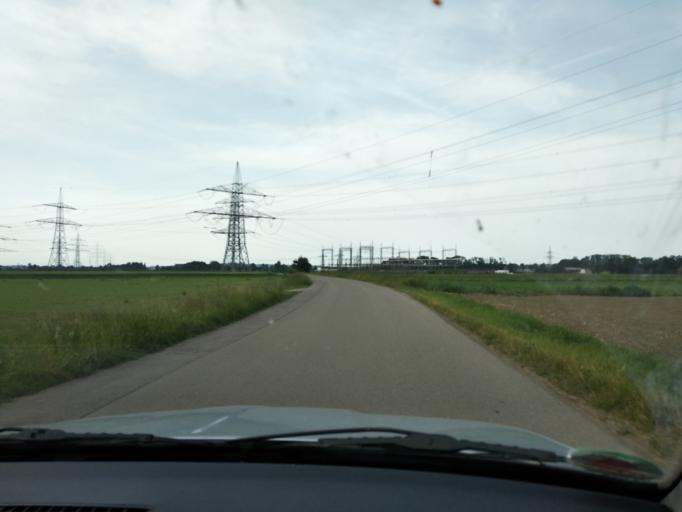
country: DE
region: Bavaria
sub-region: Swabia
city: Woringen
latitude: 47.9337
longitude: 10.2118
